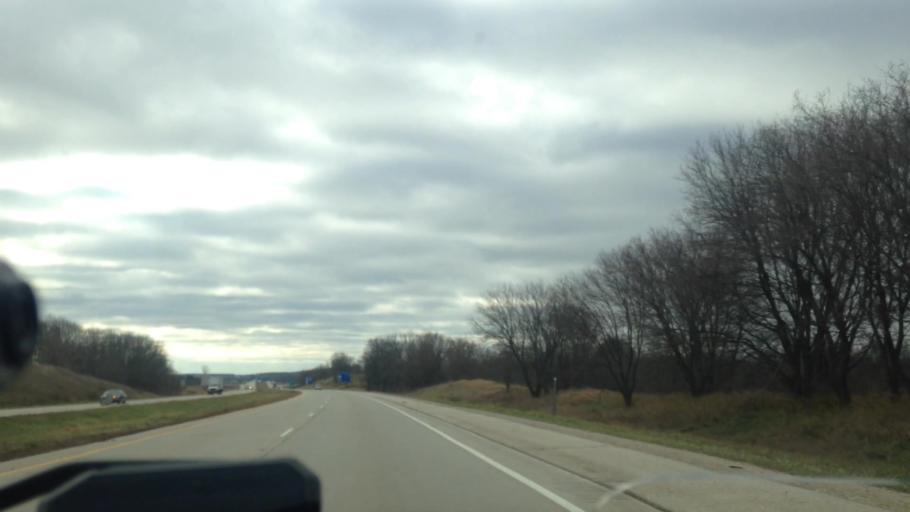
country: US
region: Wisconsin
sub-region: Washington County
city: Jackson
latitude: 43.3375
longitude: -88.1905
